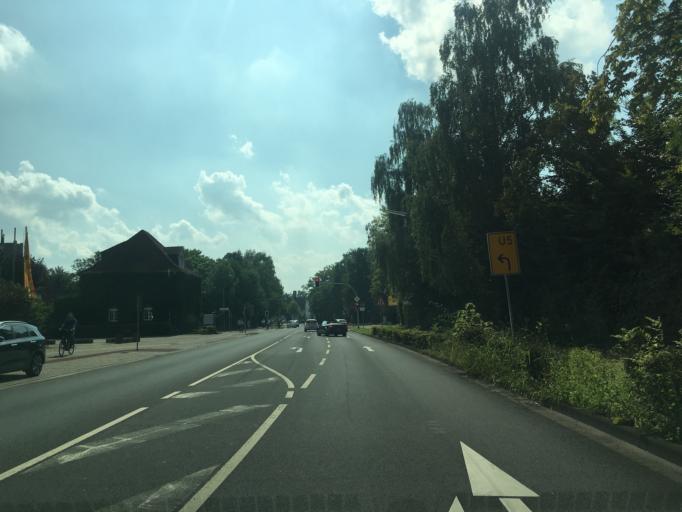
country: DE
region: North Rhine-Westphalia
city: Selm
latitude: 51.6953
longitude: 7.4664
